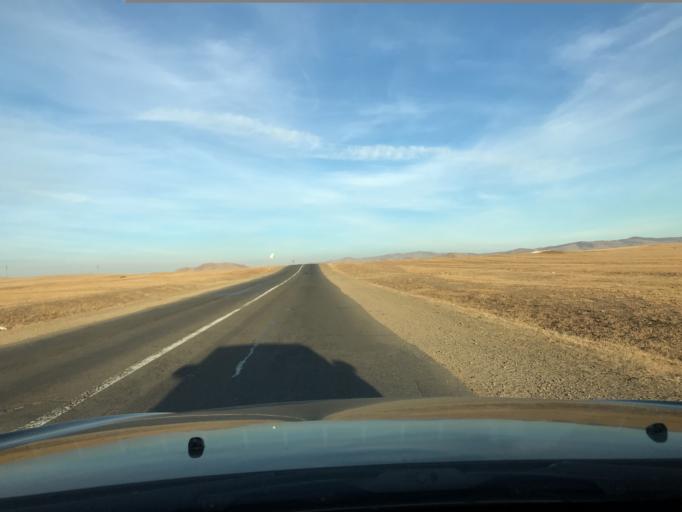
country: MN
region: Central Aimak
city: Arhust
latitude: 47.7754
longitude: 107.4221
